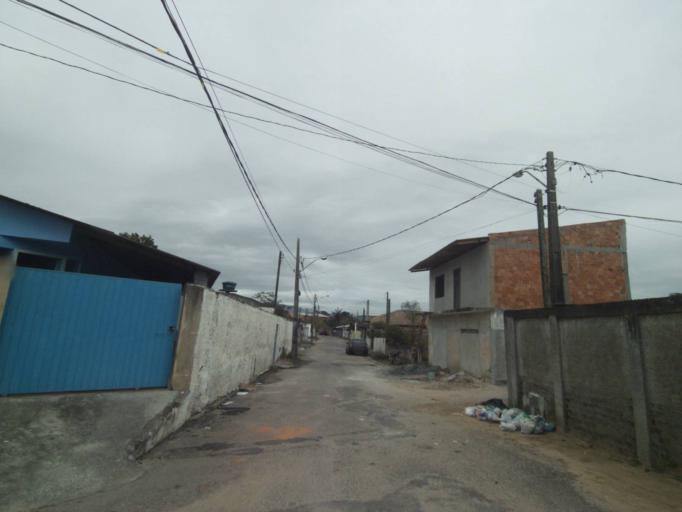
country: BR
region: Parana
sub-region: Paranagua
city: Paranagua
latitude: -25.5202
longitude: -48.5332
